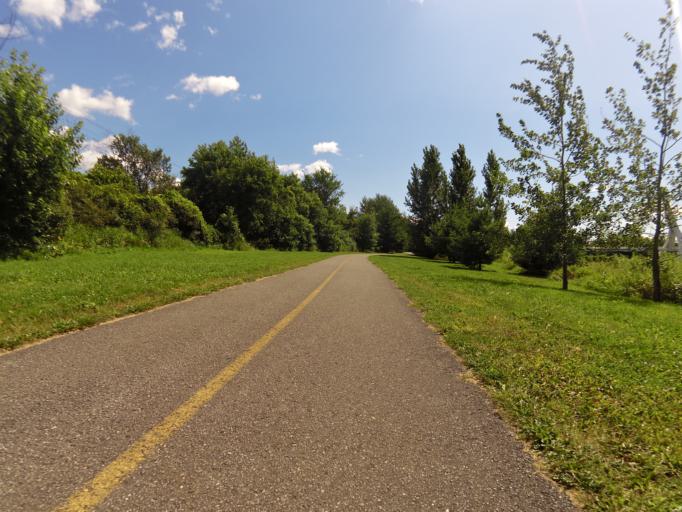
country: CA
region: Ontario
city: Ottawa
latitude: 45.3557
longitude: -75.6573
